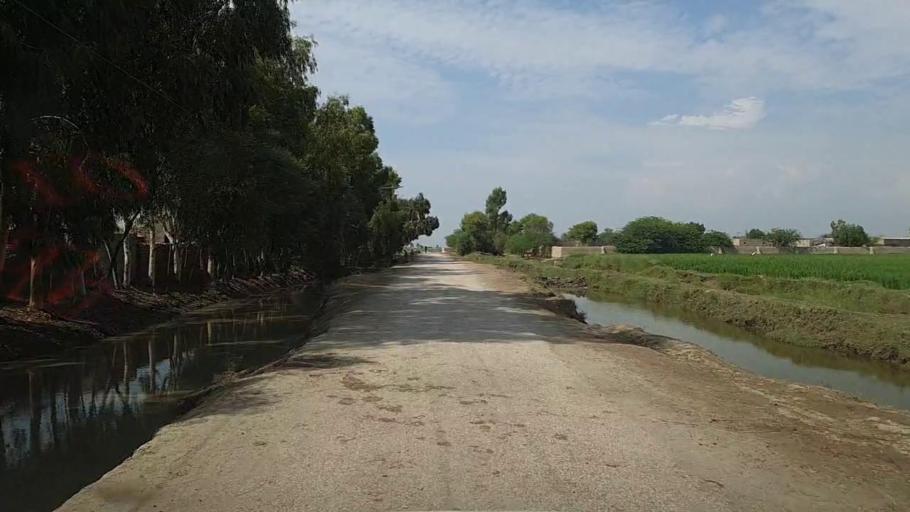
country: PK
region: Sindh
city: Thul
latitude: 28.2528
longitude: 68.8074
